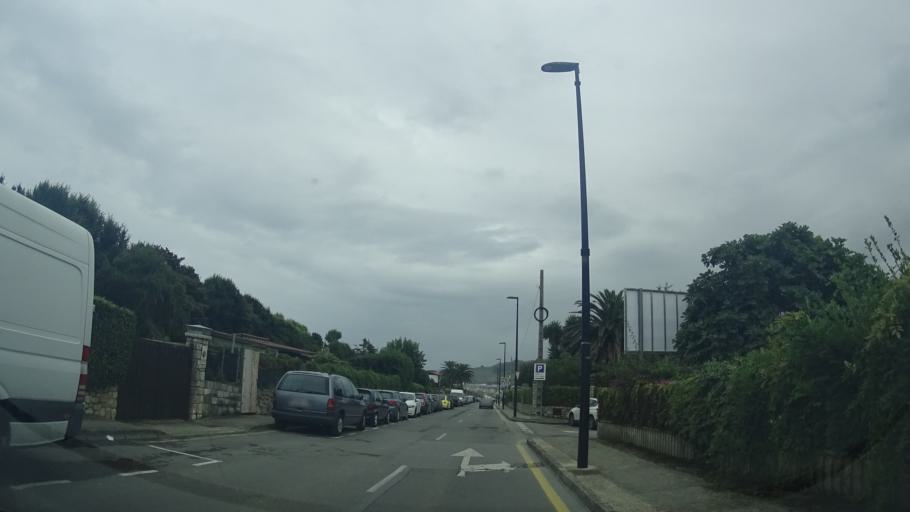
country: ES
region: Asturias
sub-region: Province of Asturias
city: Llanes
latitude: 43.4240
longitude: -4.7563
